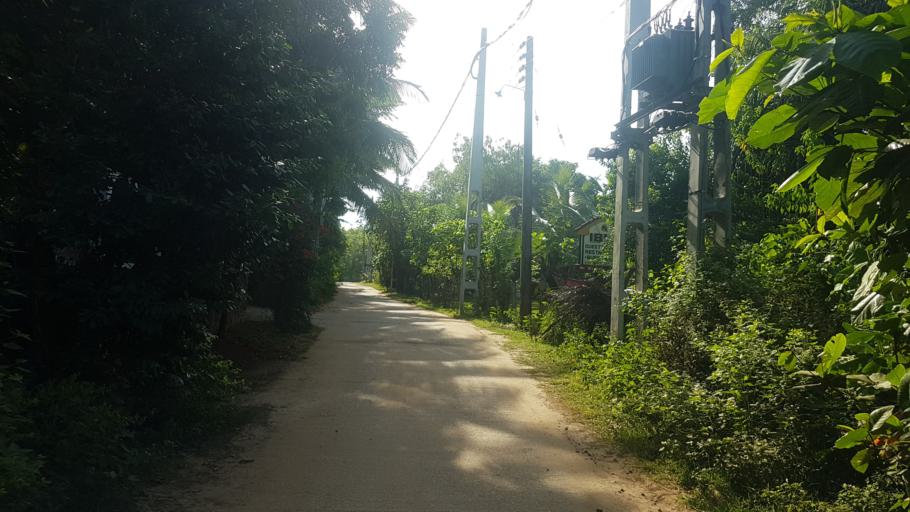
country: LK
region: Southern
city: Tangalla
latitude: 6.0393
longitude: 80.8101
